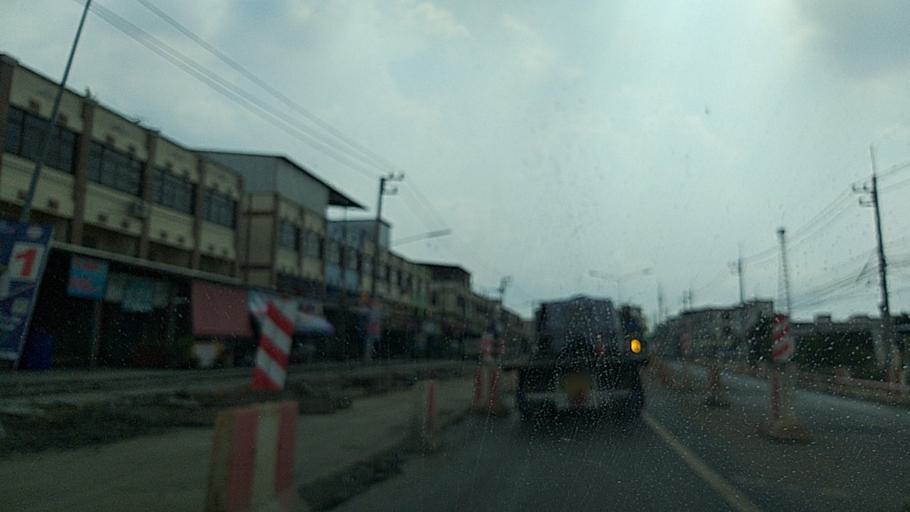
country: TH
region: Chon Buri
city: Ban Bueng
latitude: 13.2940
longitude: 101.1763
